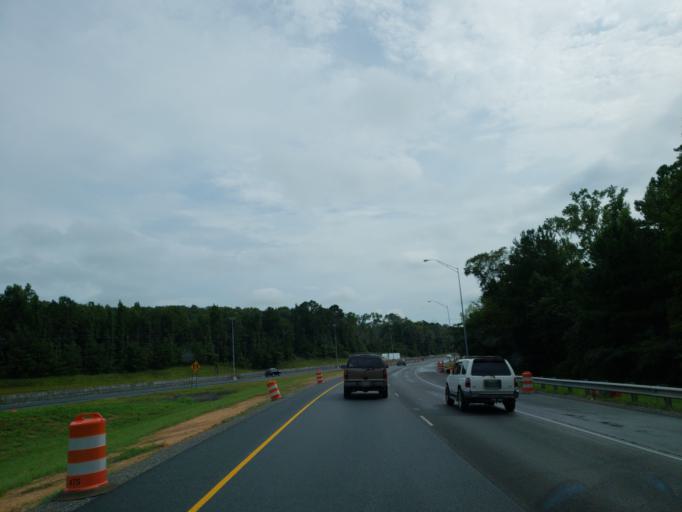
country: US
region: Alabama
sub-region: Jefferson County
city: Bessemer
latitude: 33.3369
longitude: -87.0348
